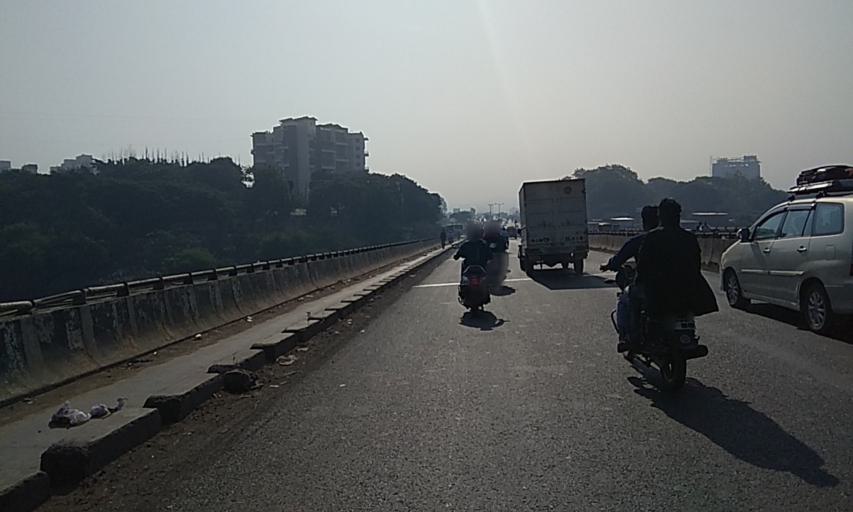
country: IN
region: Maharashtra
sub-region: Pune Division
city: Kharakvasla
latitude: 18.4751
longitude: 73.8090
